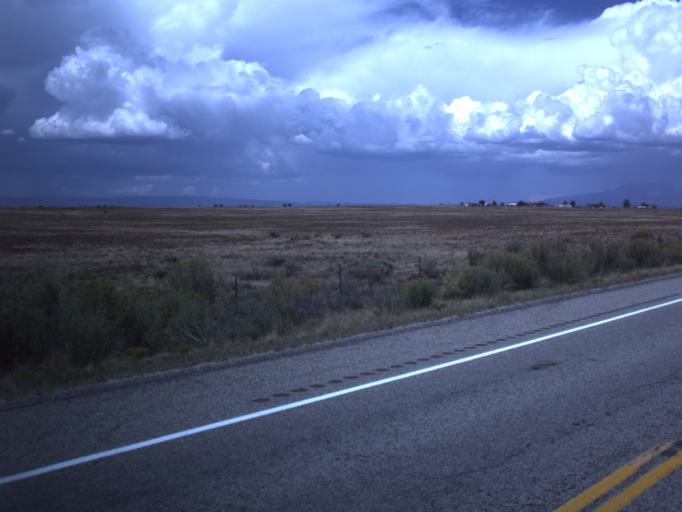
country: US
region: Utah
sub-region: San Juan County
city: Blanding
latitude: 37.4455
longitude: -109.4674
